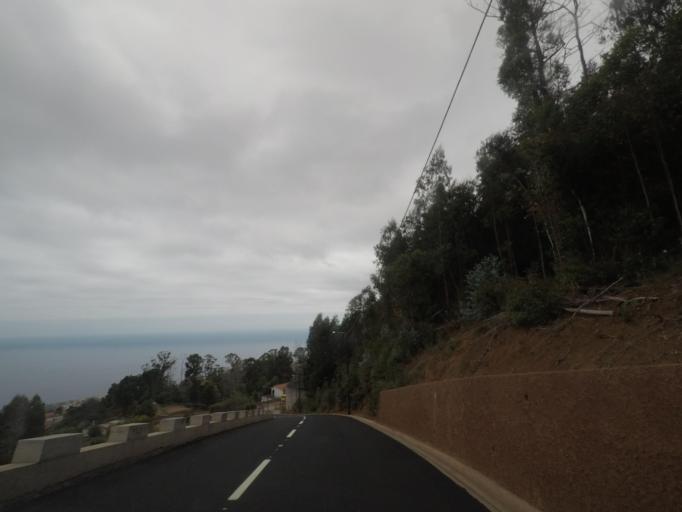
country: PT
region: Madeira
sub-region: Calheta
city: Estreito da Calheta
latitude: 32.7414
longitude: -17.1628
